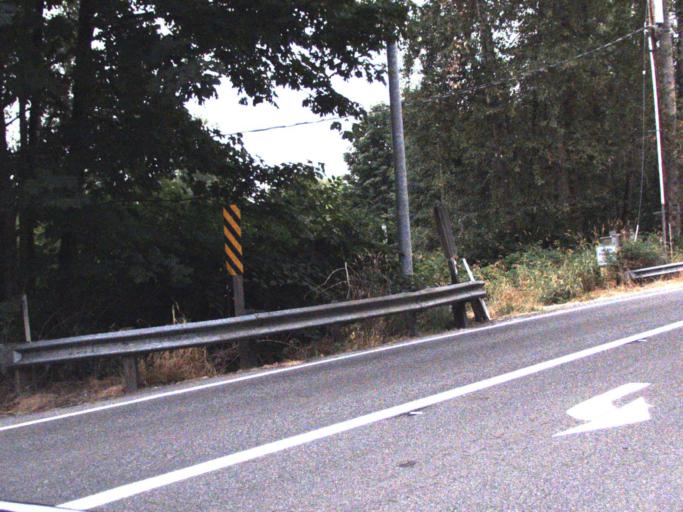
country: US
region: Washington
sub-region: King County
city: Lake Marcel-Stillwater
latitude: 47.6830
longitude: -121.9206
